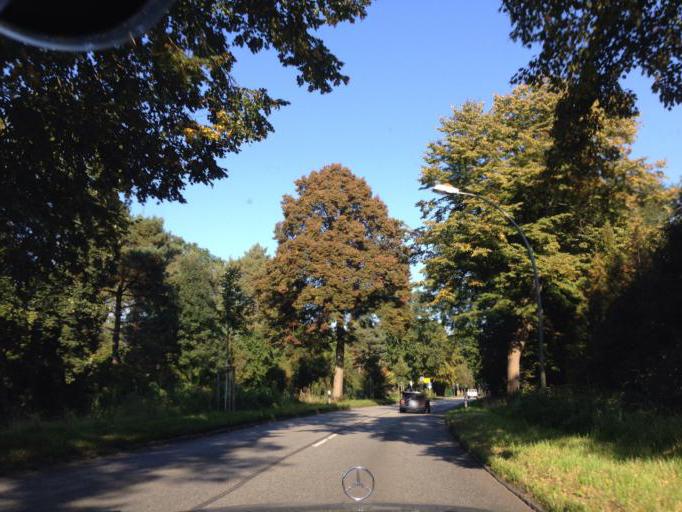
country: DE
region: Schleswig-Holstein
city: Ahrensburg
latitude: 53.6620
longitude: 10.2172
